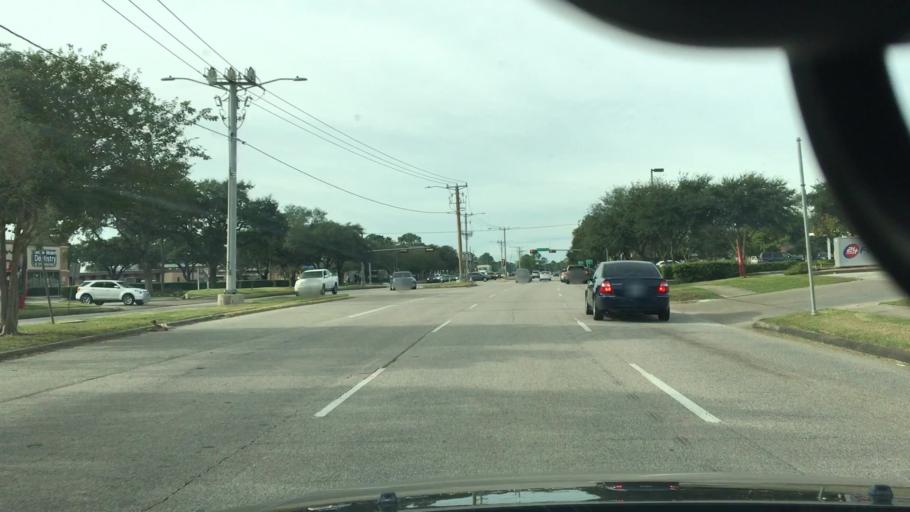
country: US
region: Texas
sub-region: Harris County
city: Webster
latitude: 29.5557
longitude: -95.1192
